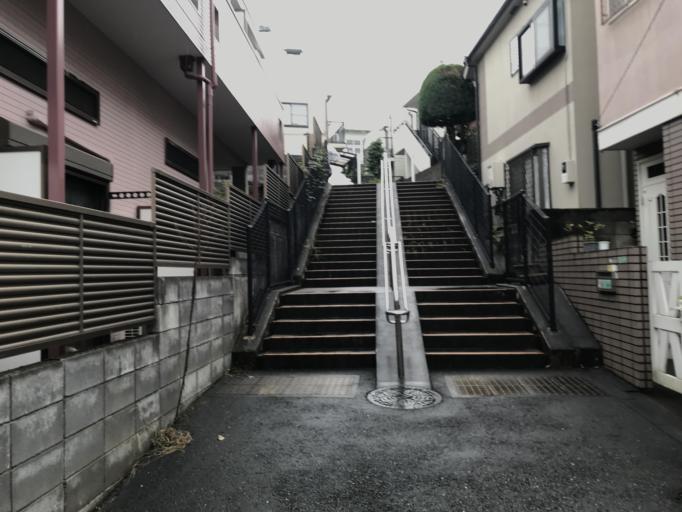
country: JP
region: Saitama
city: Wako
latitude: 35.7409
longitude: 139.6402
